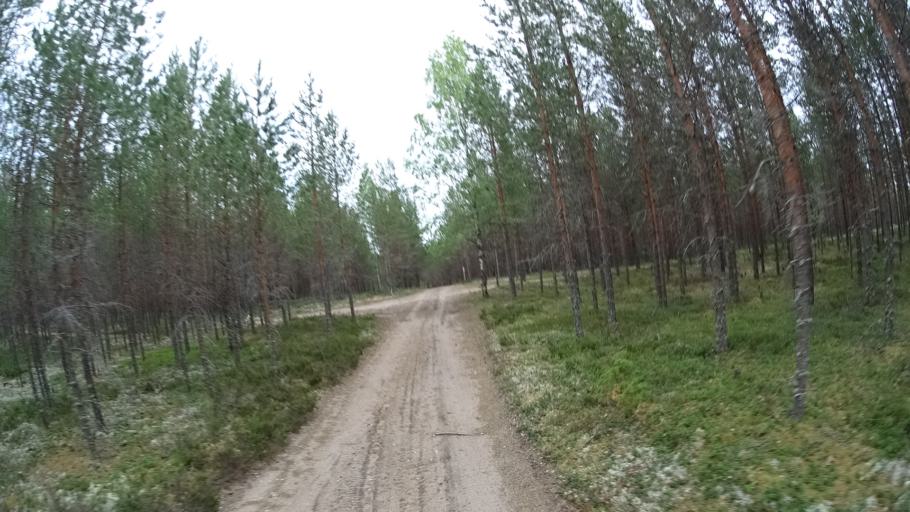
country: FI
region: Satakunta
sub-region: Pohjois-Satakunta
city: Jaemijaervi
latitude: 61.7624
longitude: 22.7734
